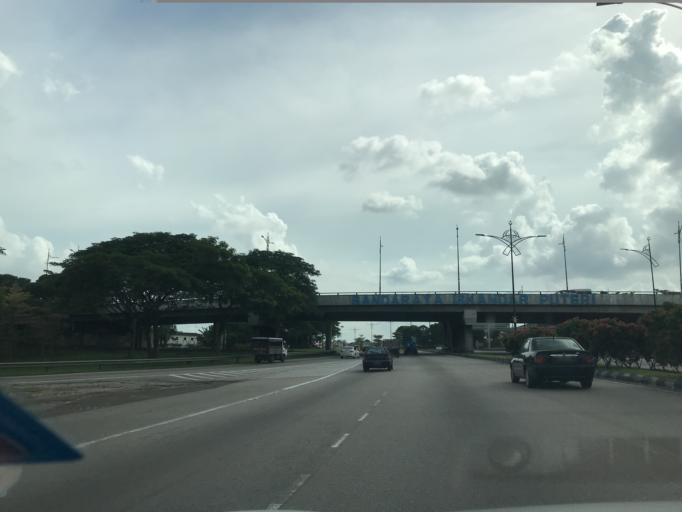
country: MY
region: Johor
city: Skudai
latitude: 1.5493
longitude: 103.6574
